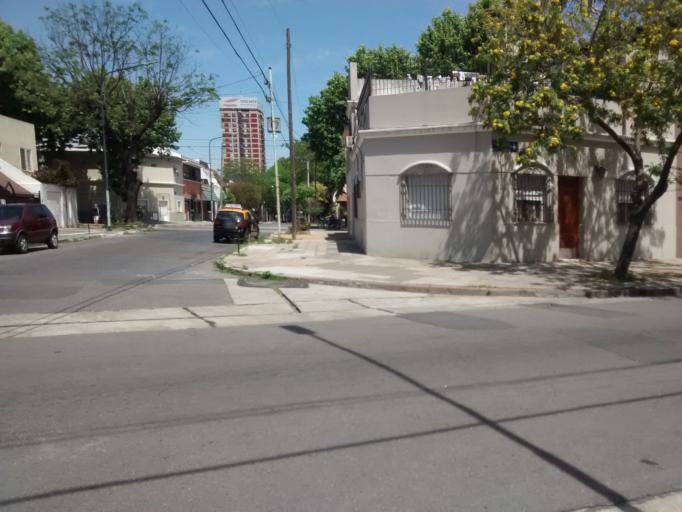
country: AR
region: Buenos Aires
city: Caseros
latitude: -34.6319
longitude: -58.5267
